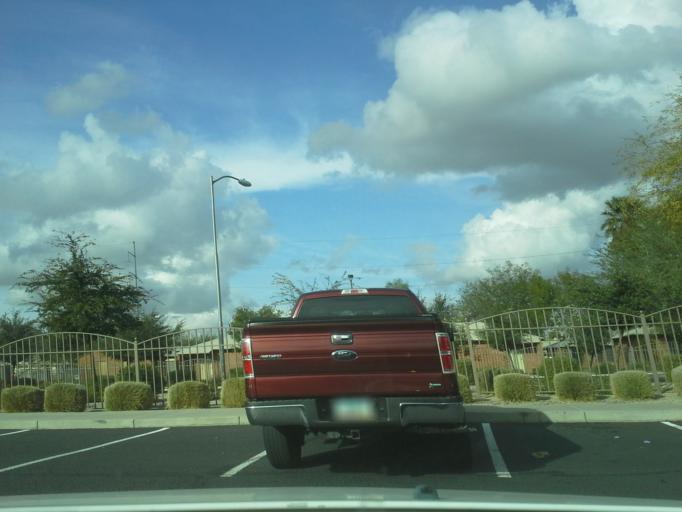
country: US
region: Arizona
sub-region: Maricopa County
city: Phoenix
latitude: 33.4387
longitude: -112.0832
